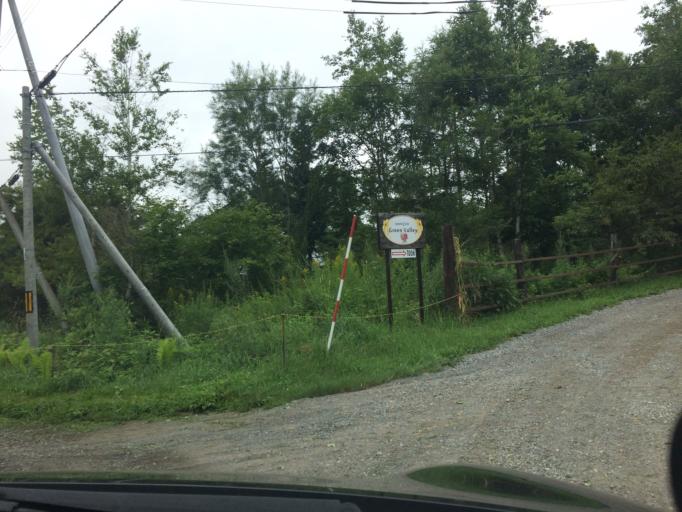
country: JP
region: Hokkaido
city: Otofuke
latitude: 42.9627
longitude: 143.1206
